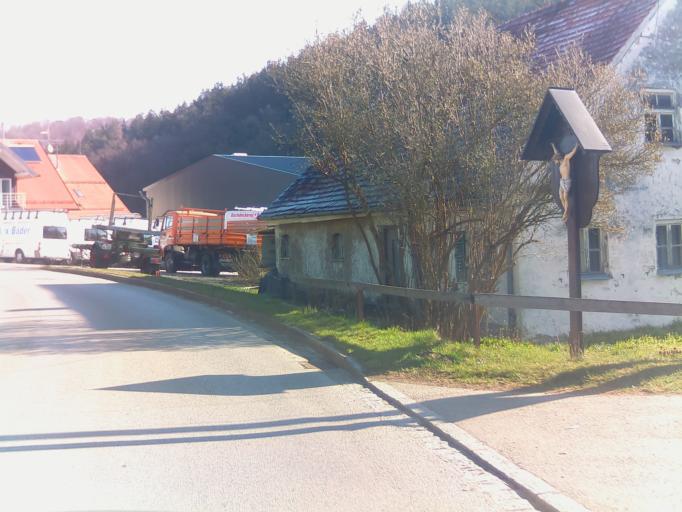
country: DE
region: Bavaria
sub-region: Swabia
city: Fischach
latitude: 48.2786
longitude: 10.7049
